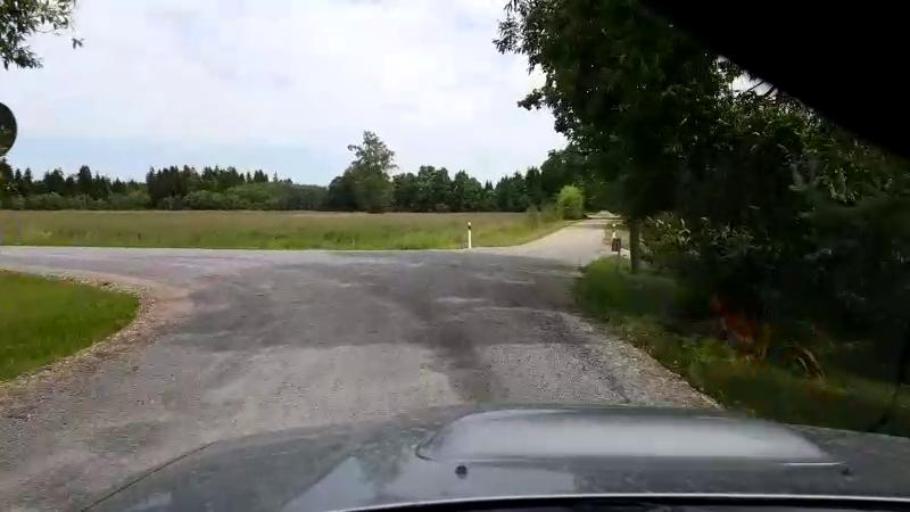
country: EE
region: Paernumaa
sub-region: Tootsi vald
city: Tootsi
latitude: 58.5408
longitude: 24.7357
